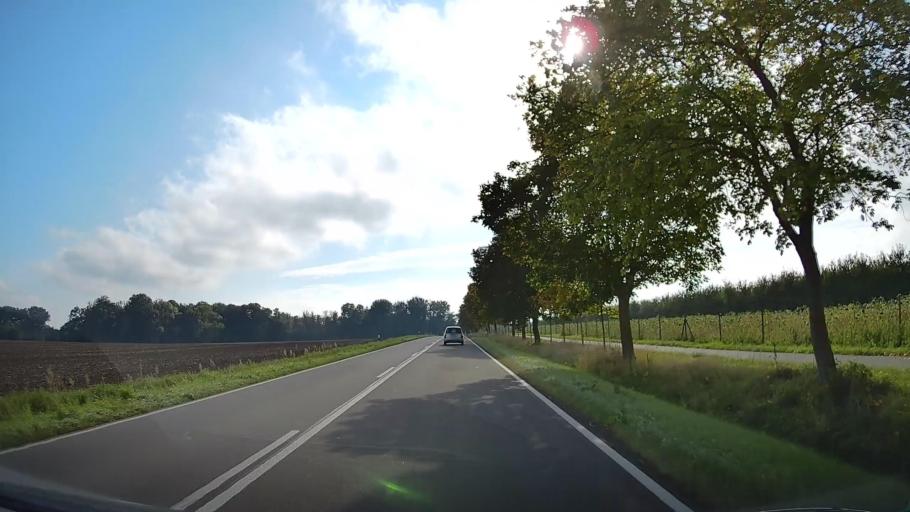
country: DE
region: Mecklenburg-Vorpommern
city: Lubtheen
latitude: 53.3863
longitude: 11.0868
